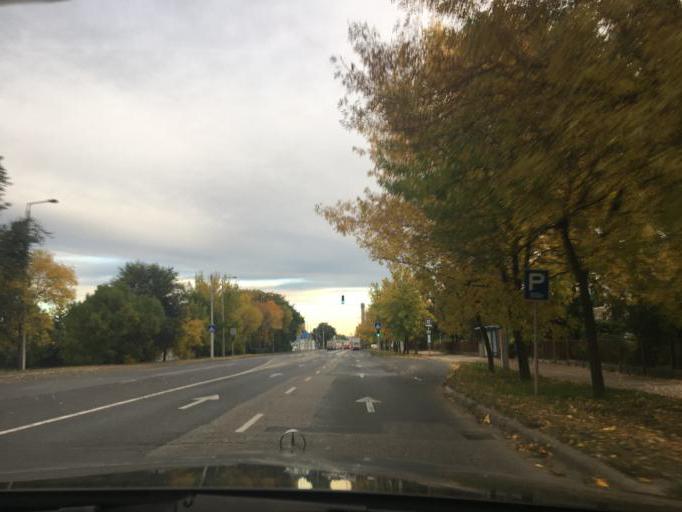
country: HU
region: Hajdu-Bihar
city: Debrecen
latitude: 47.5086
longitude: 21.6302
